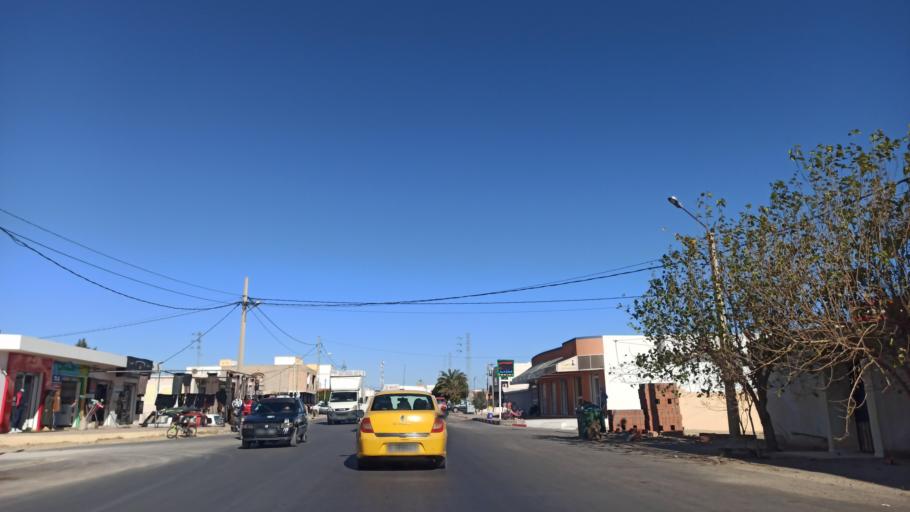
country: TN
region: Sidi Bu Zayd
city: Bi'r al Hufayy
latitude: 34.9224
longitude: 9.1888
